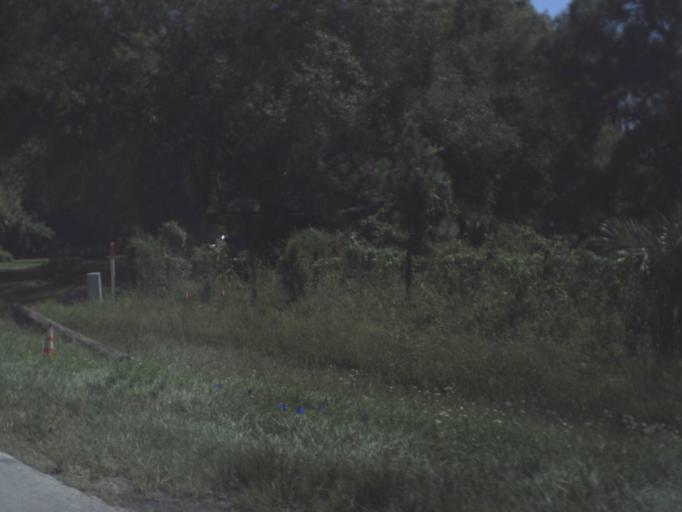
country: US
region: Florida
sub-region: Okeechobee County
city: Cypress Quarters
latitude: 27.2439
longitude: -80.7939
